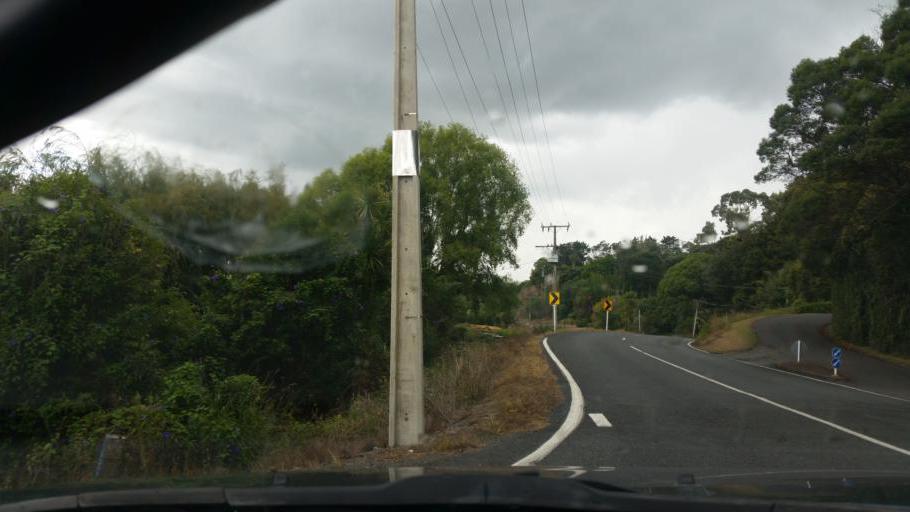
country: NZ
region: Northland
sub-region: Kaipara District
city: Dargaville
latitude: -35.9541
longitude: 173.8591
